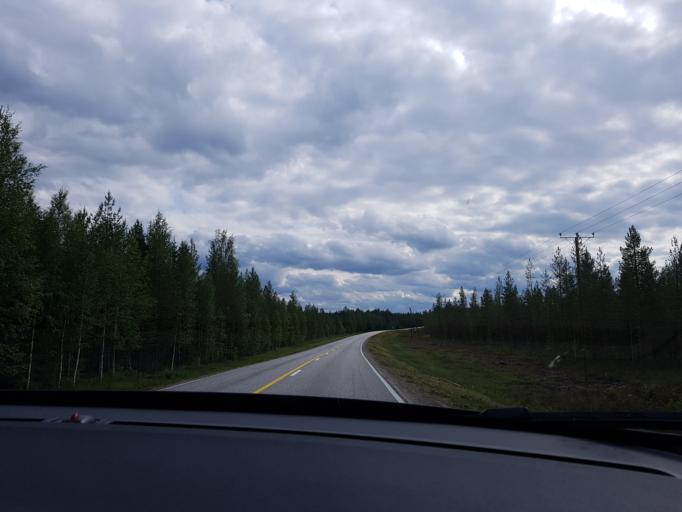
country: FI
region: Kainuu
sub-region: Kehys-Kainuu
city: Kuhmo
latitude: 64.3357
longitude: 29.8773
